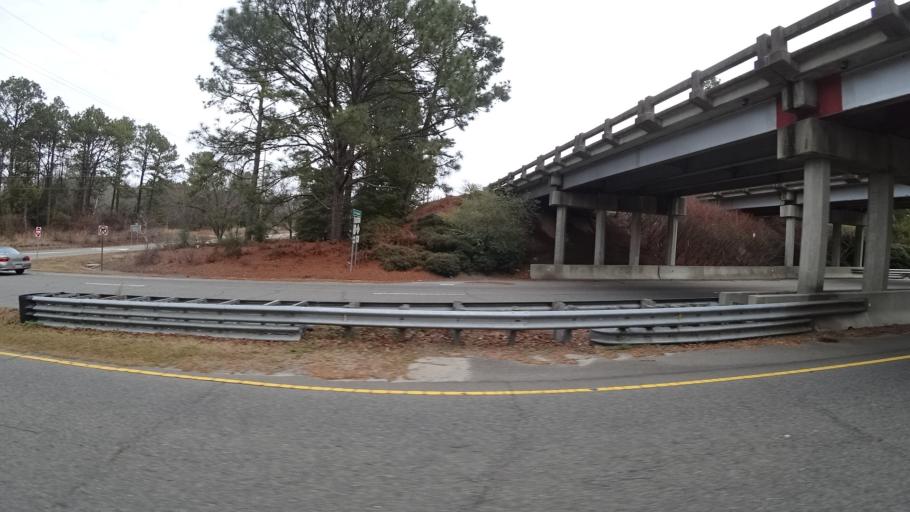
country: US
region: North Carolina
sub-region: Moore County
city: Southern Pines
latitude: 35.1911
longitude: -79.3849
